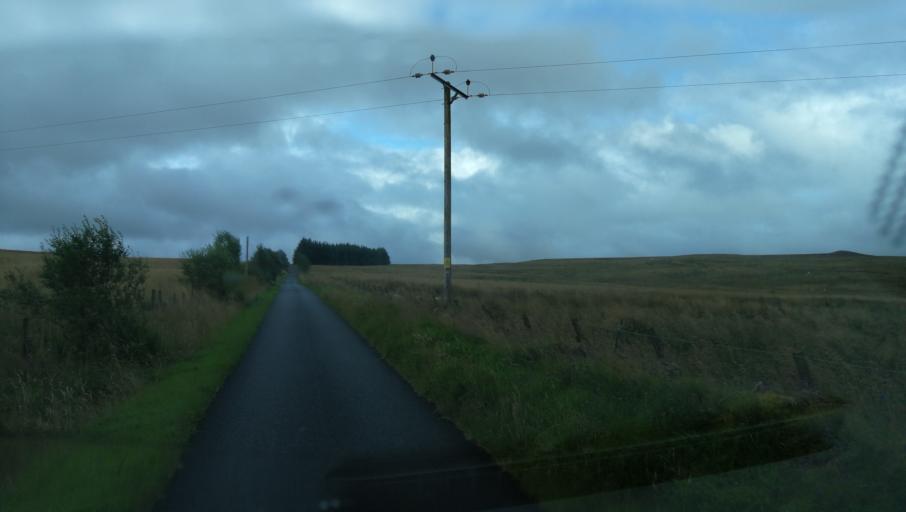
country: GB
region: Scotland
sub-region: Perth and Kinross
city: Blairgowrie
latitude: 56.6877
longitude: -3.3872
